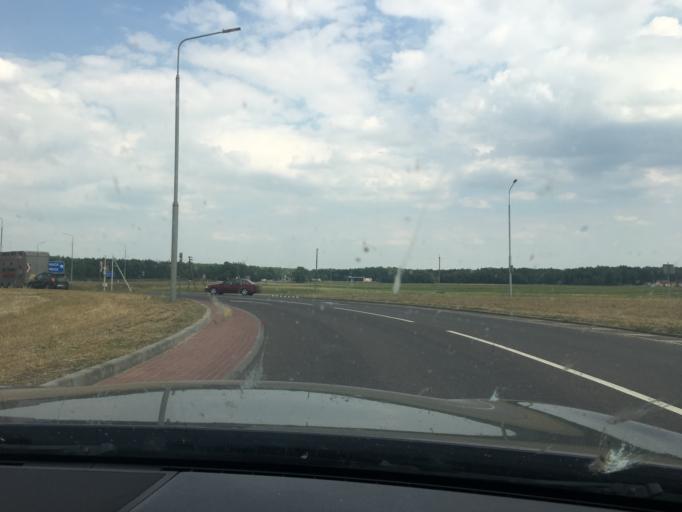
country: BY
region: Brest
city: Brest
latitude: 52.1513
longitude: 23.6912
